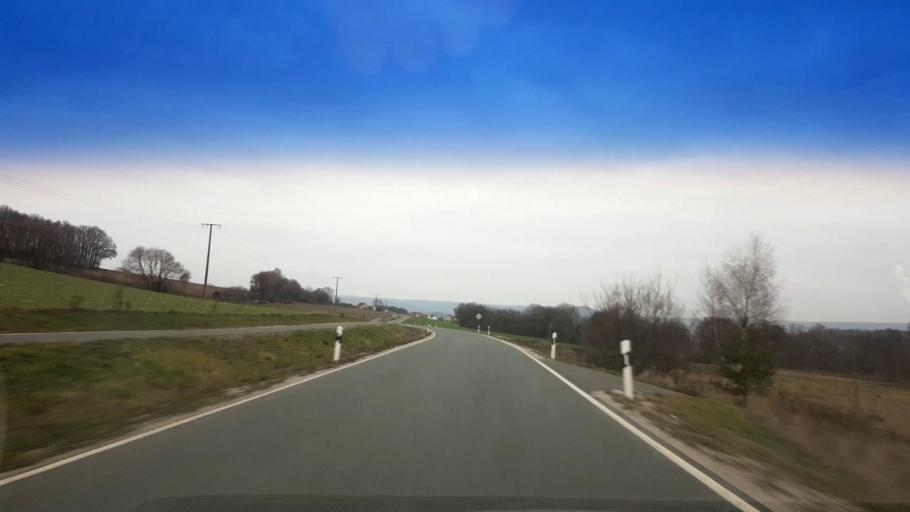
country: DE
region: Bavaria
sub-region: Upper Franconia
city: Hallerndorf
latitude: 49.7664
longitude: 10.9909
